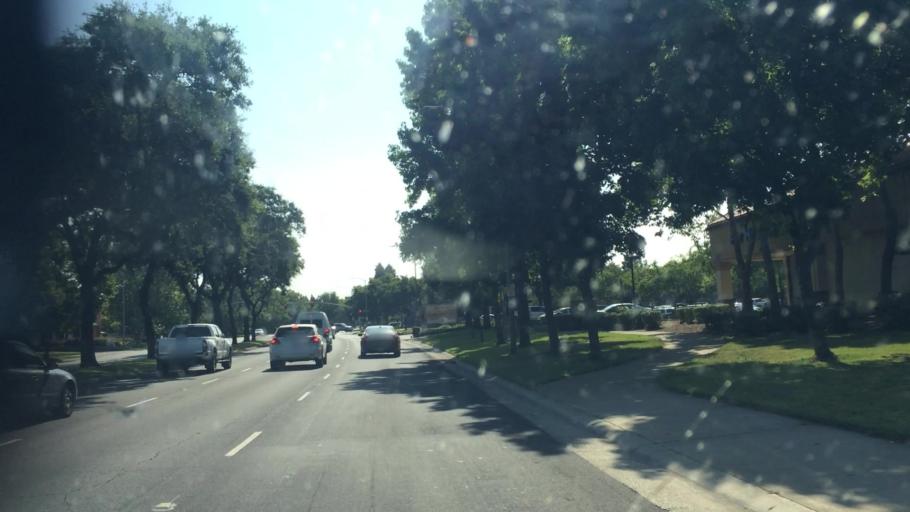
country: US
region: California
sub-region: Sacramento County
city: Laguna
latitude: 38.4231
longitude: -121.4467
